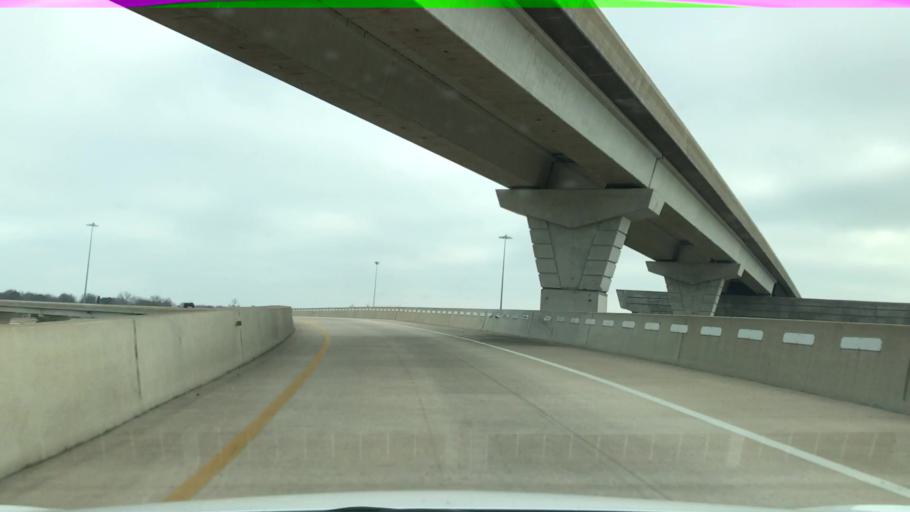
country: US
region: Texas
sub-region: Dallas County
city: Rowlett
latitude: 32.8606
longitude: -96.5555
